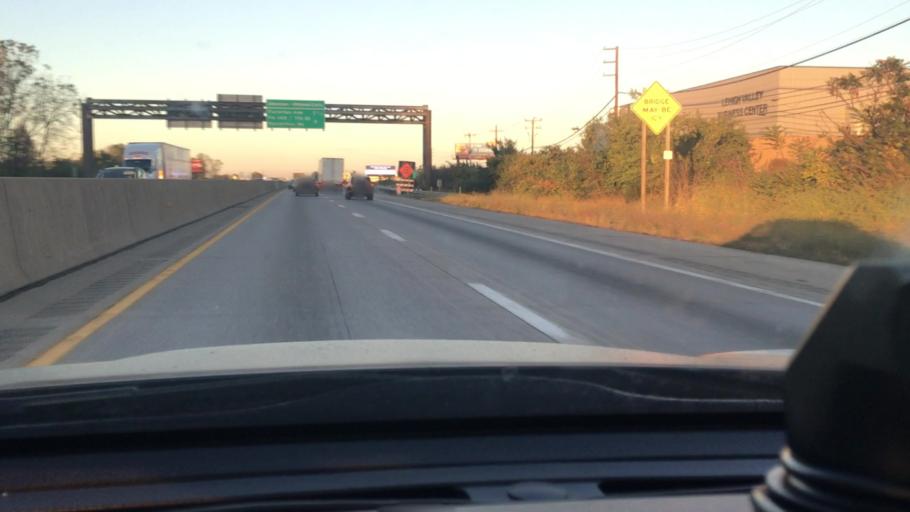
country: US
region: Pennsylvania
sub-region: Lehigh County
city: Fullerton
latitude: 40.6389
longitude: -75.4450
